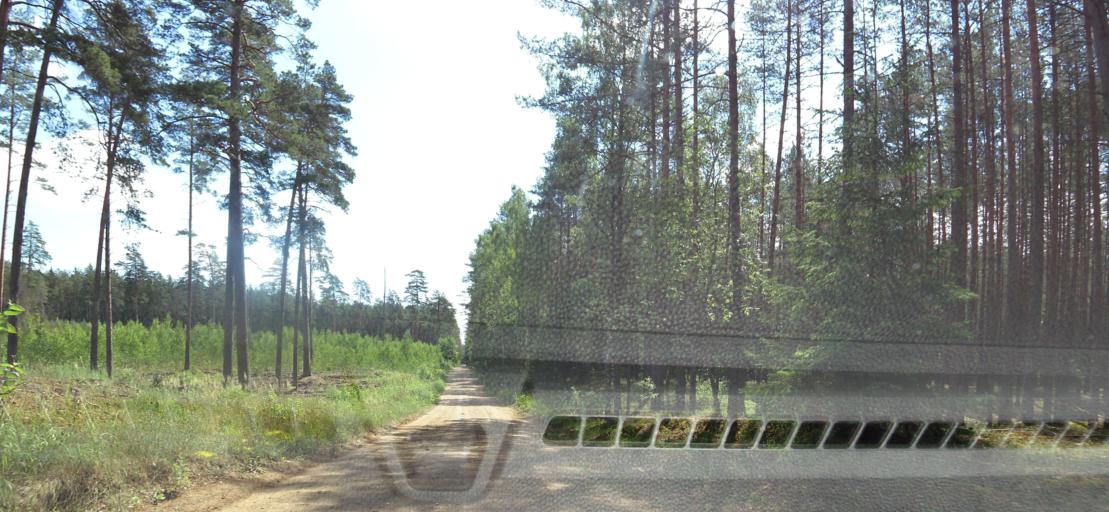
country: LT
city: Nemencine
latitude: 54.8313
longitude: 25.4375
